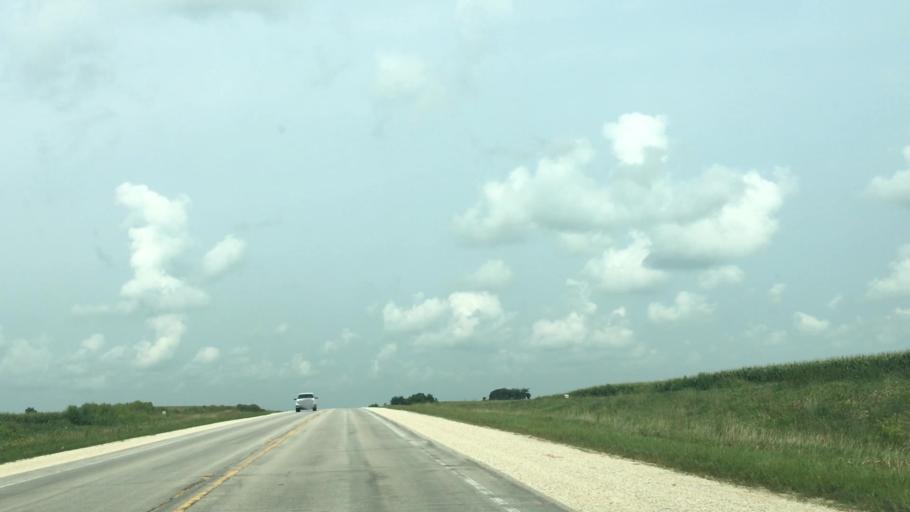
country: US
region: Iowa
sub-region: Winneshiek County
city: Decorah
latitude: 43.3811
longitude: -91.8205
